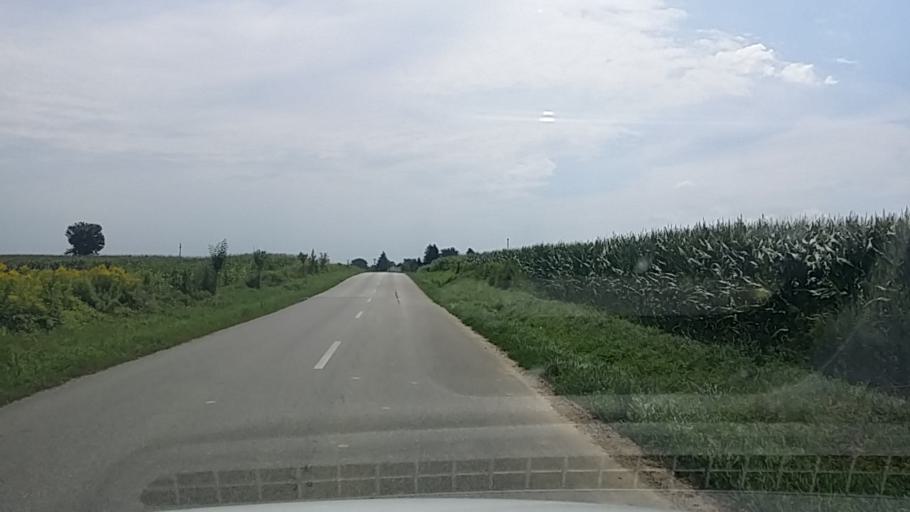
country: HU
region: Zala
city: Becsehely
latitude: 46.4073
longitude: 16.7844
